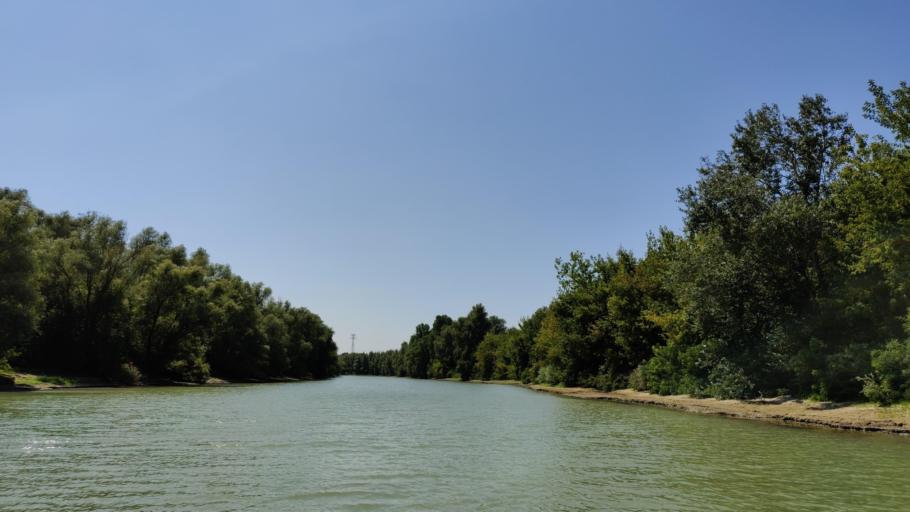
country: RO
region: Tulcea
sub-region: Municipiul Tulcea
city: Tulcea
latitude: 45.2103
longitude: 28.8590
